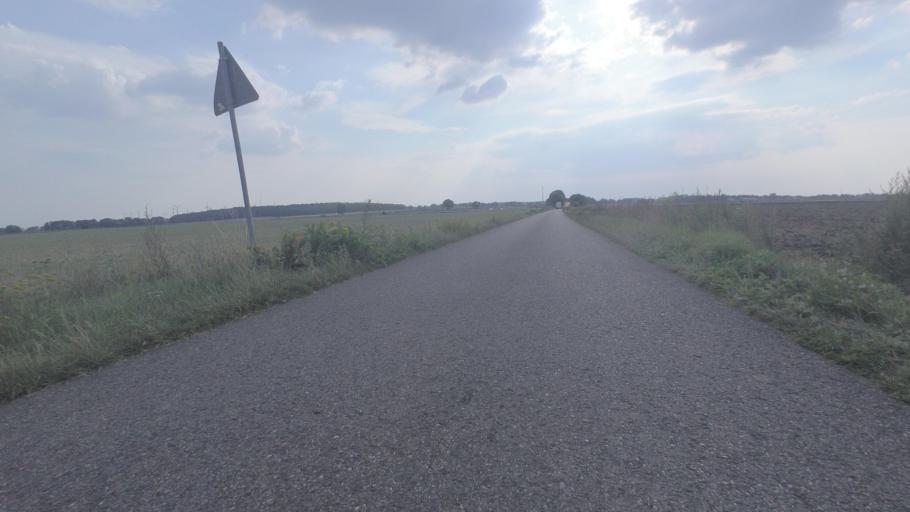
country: DE
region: Brandenburg
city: Wittstock
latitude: 53.2417
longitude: 12.4562
